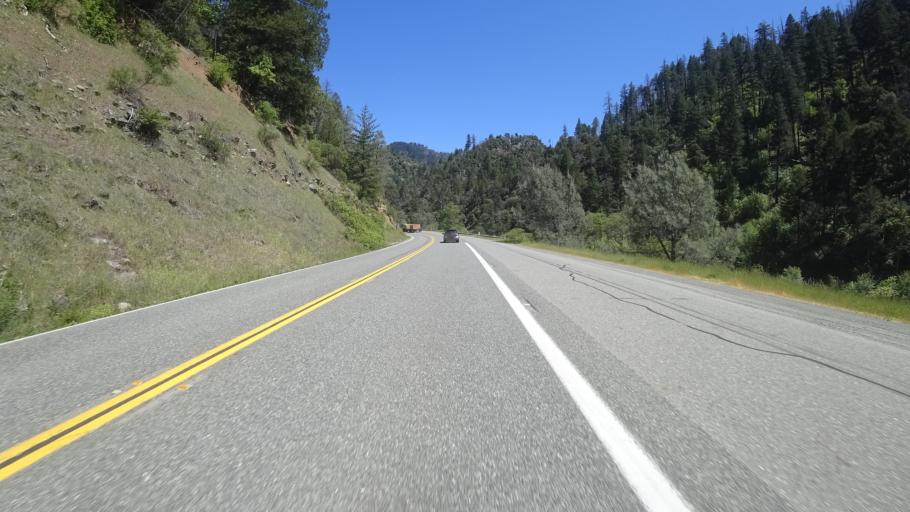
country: US
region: California
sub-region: Trinity County
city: Hayfork
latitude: 40.7661
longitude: -123.3038
